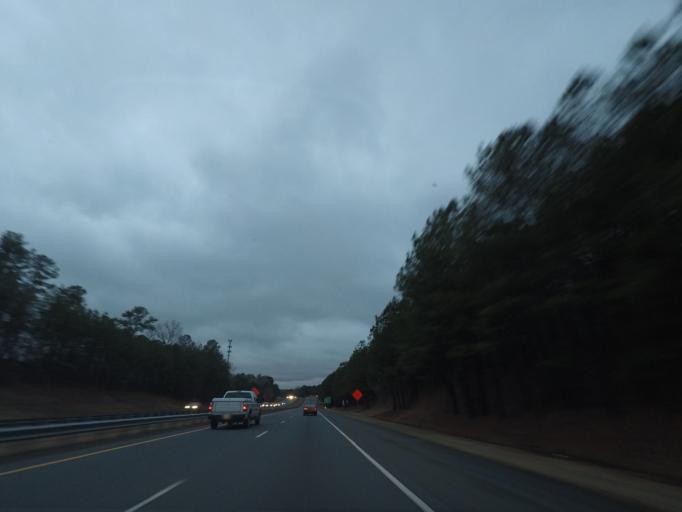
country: US
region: North Carolina
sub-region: Chatham County
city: Pittsboro
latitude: 35.6276
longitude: -79.0799
